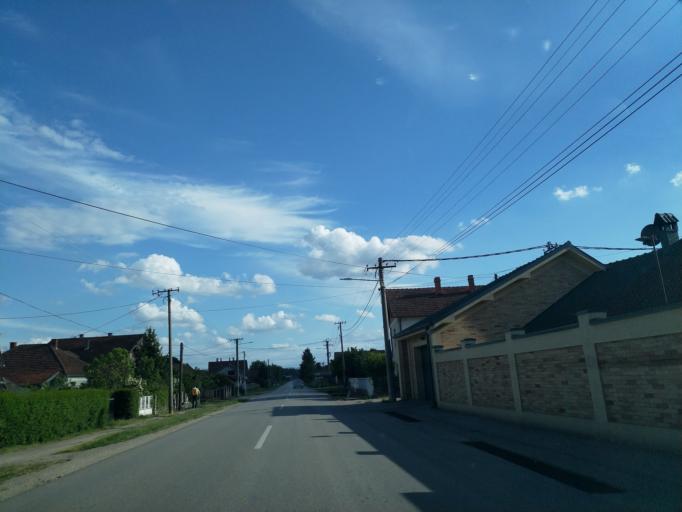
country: RS
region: Central Serbia
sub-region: Sumadijski Okrug
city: Lapovo
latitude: 44.1841
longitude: 21.0917
